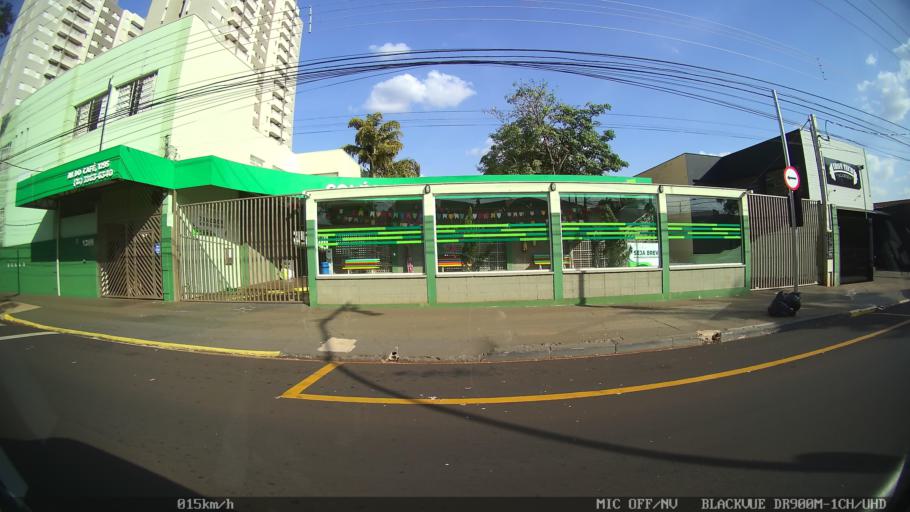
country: BR
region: Sao Paulo
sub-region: Ribeirao Preto
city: Ribeirao Preto
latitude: -21.1749
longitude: -47.8304
